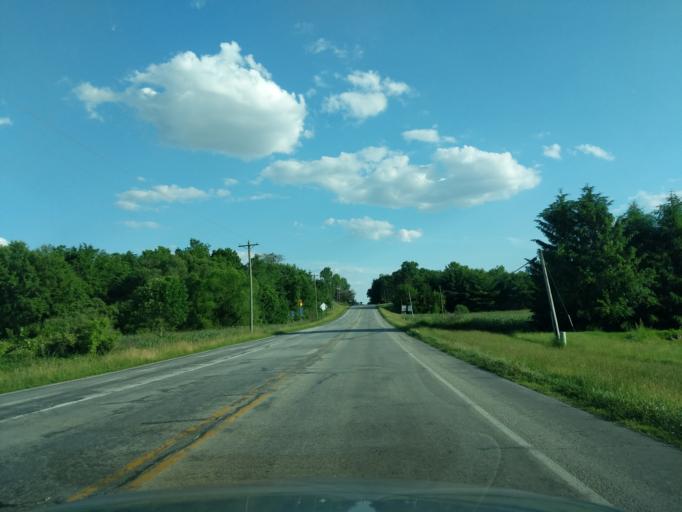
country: US
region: Indiana
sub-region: Whitley County
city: Columbia City
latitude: 41.1324
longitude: -85.4814
